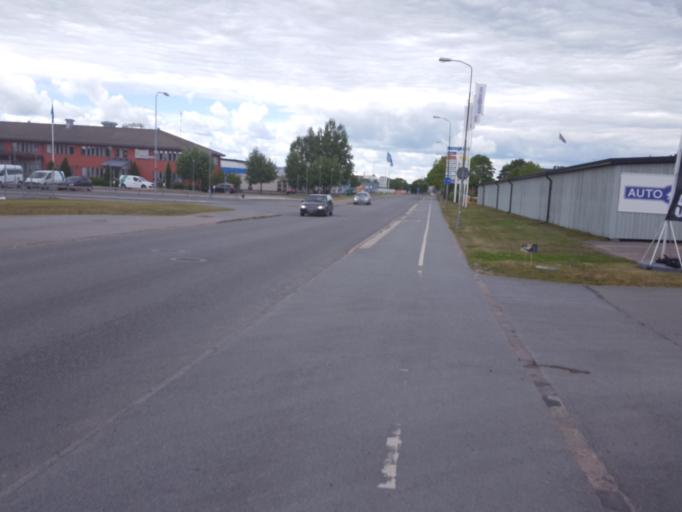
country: SE
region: Uppsala
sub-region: Uppsala Kommun
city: Saevja
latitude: 59.8481
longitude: 17.6853
